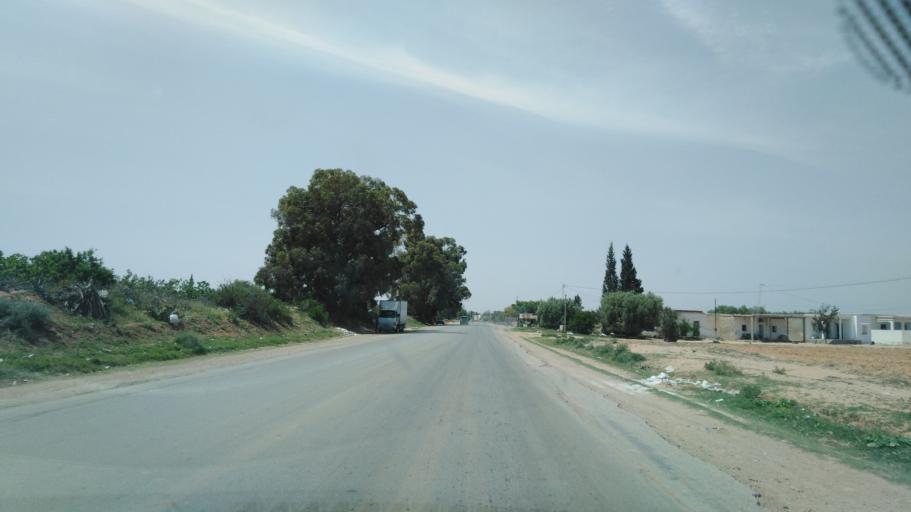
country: TN
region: Safaqis
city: Sfax
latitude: 34.7320
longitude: 10.5586
